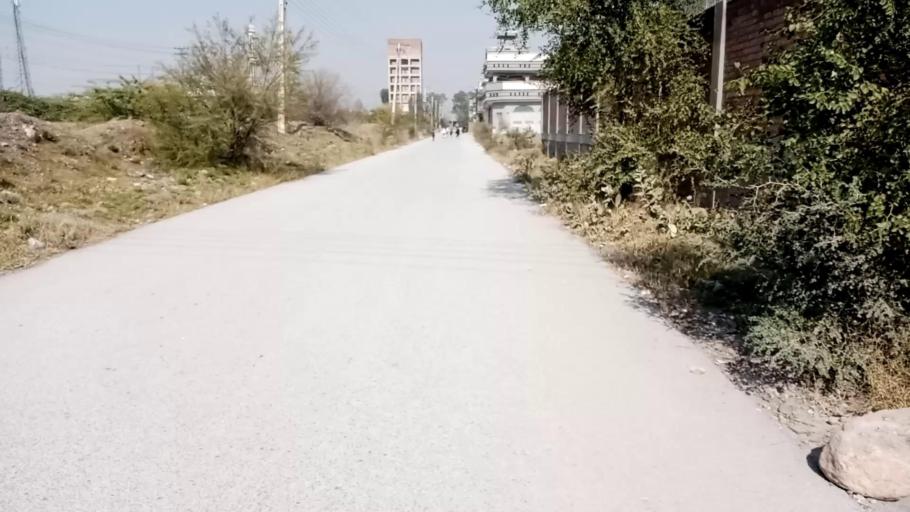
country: PK
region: Khyber Pakhtunkhwa
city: Peshawar
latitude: 33.9624
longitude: 71.4128
